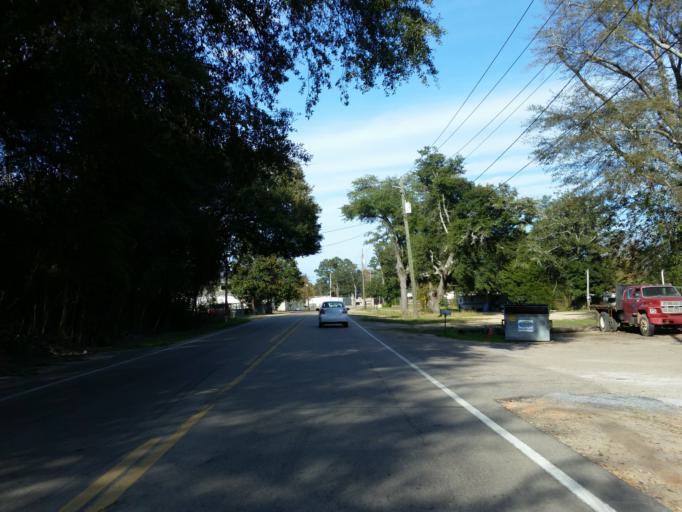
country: US
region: Mississippi
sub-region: Jones County
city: Ellisville
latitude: 31.6438
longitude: -89.1777
